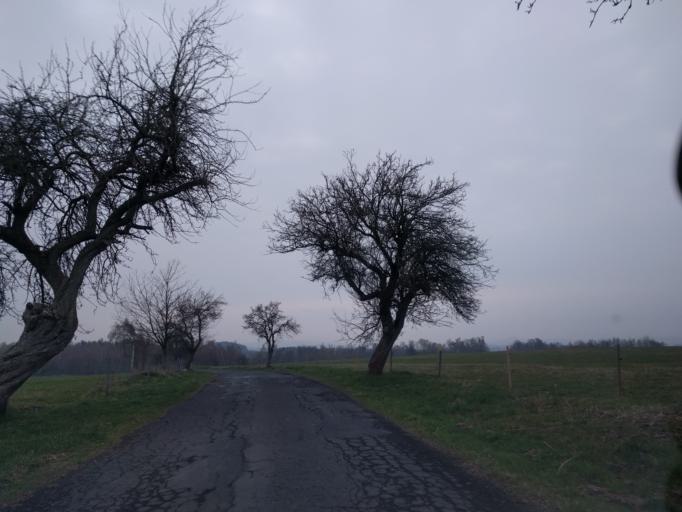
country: CZ
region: Karlovarsky
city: Bochov
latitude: 50.1237
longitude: 13.0849
